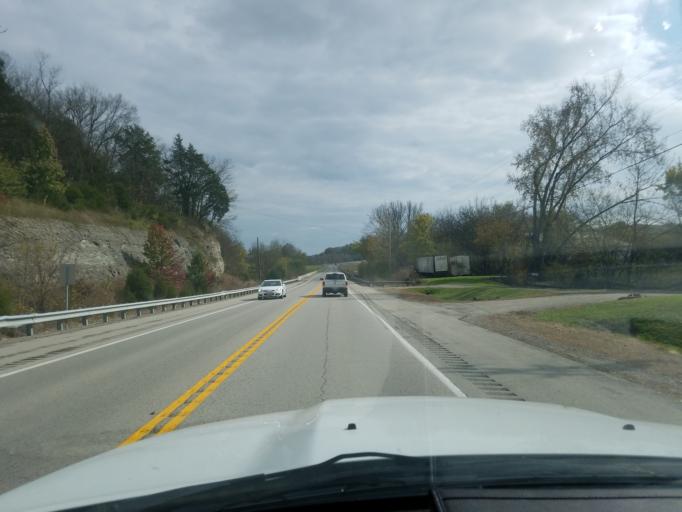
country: US
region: Kentucky
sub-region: Bullitt County
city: Mount Washington
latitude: 38.0133
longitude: -85.5143
